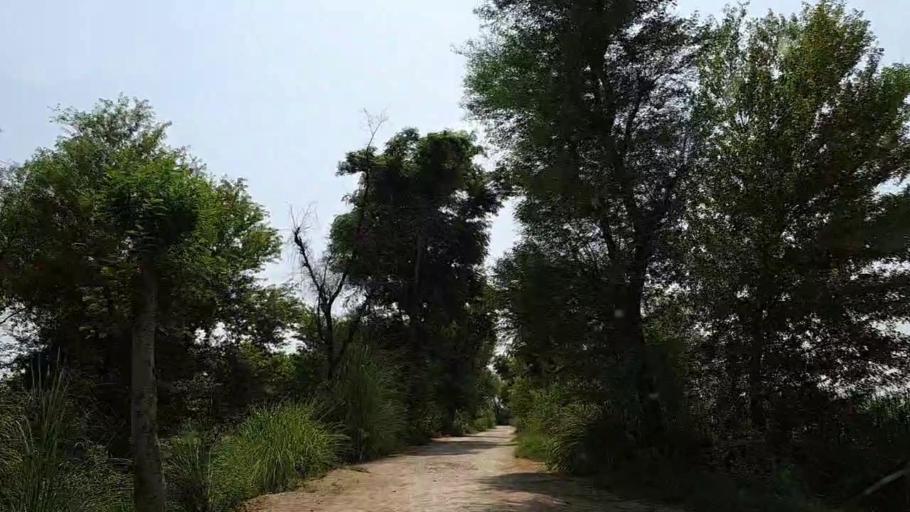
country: PK
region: Sindh
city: Adilpur
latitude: 27.9303
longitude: 69.3829
